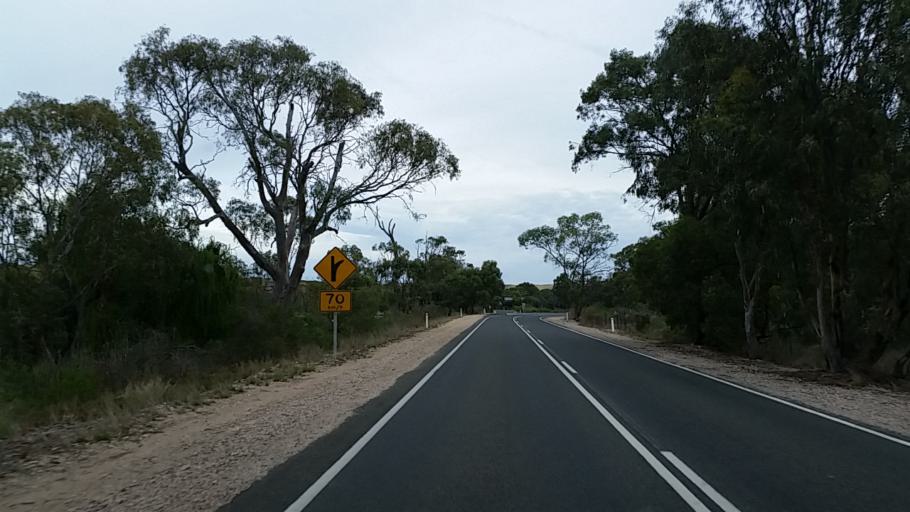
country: AU
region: South Australia
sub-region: Mid Murray
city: Mannum
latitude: -34.7603
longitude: 139.5707
